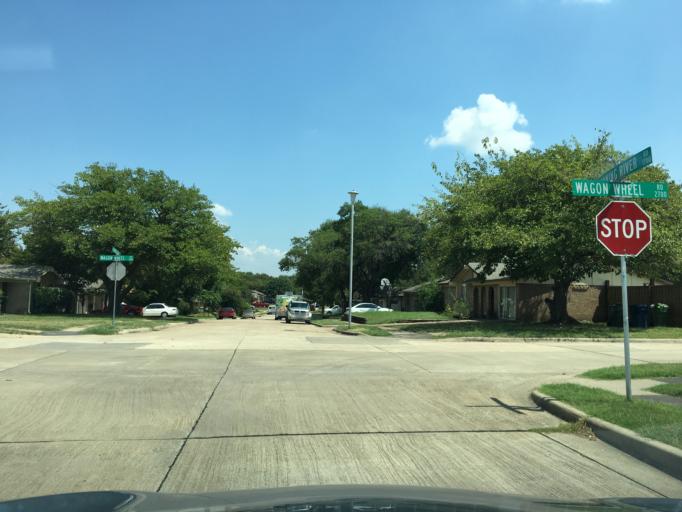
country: US
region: Texas
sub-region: Dallas County
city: Garland
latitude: 32.9429
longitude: -96.6536
